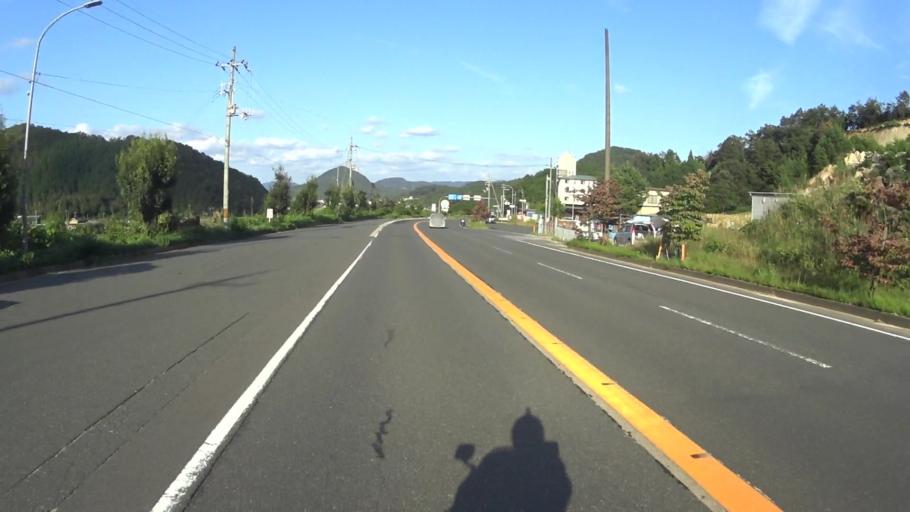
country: JP
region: Hyogo
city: Toyooka
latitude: 35.5948
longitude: 134.8804
